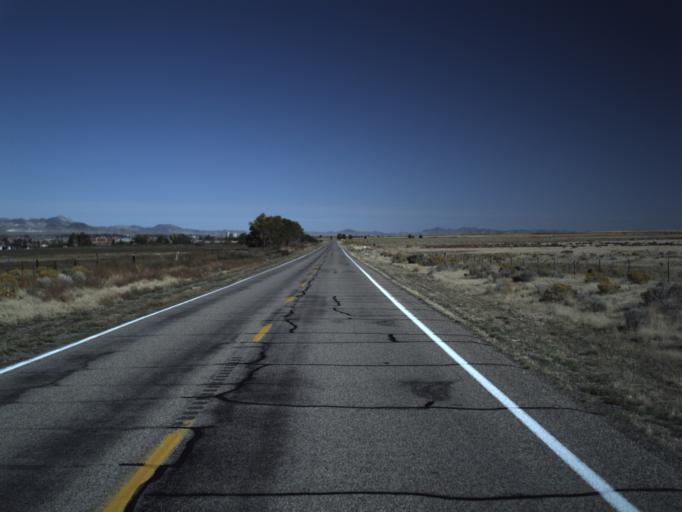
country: US
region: Utah
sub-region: Beaver County
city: Milford
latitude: 38.3257
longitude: -112.9718
